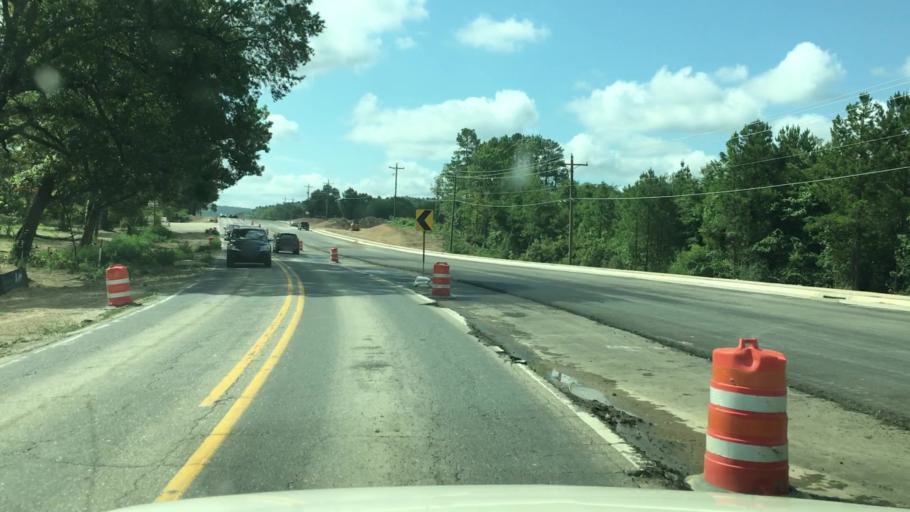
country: US
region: Arkansas
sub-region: Garland County
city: Lake Hamilton
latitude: 34.4189
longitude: -93.0980
